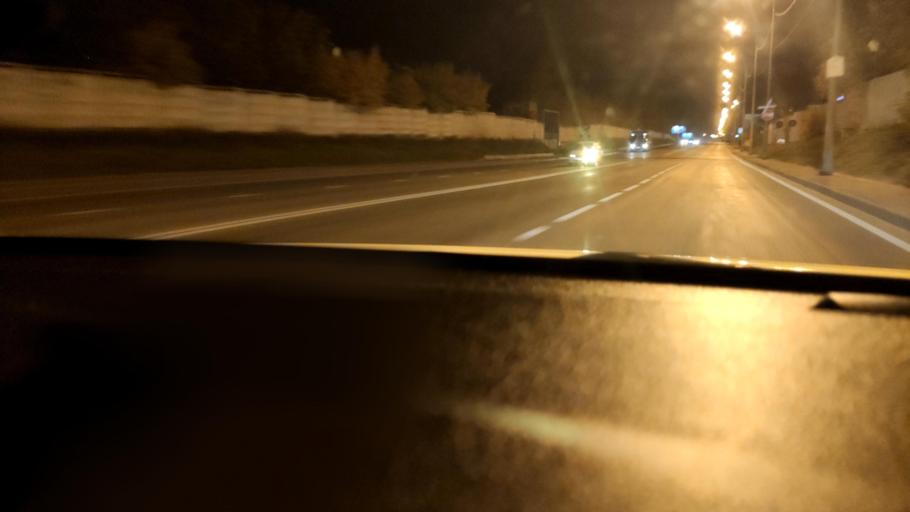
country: RU
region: Tatarstan
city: Staroye Arakchino
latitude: 55.8391
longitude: 49.0455
